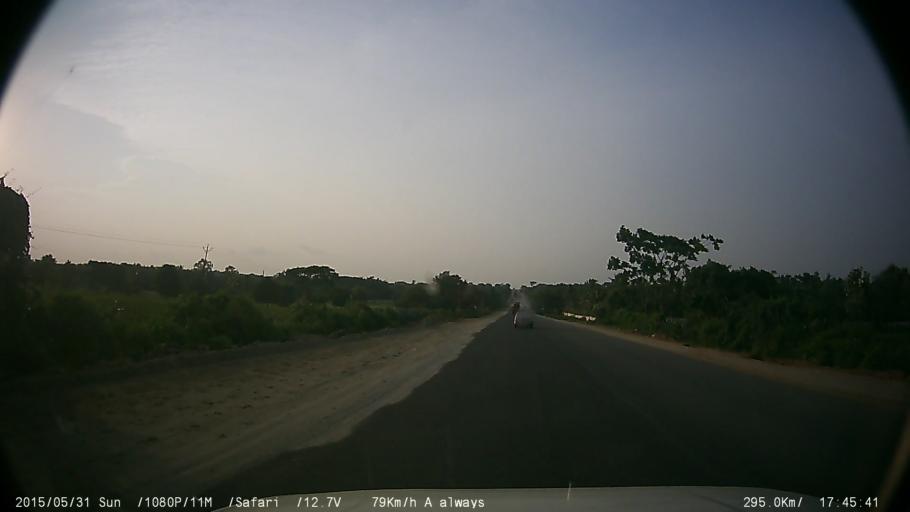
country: IN
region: Karnataka
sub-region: Chamrajnagar
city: Gundlupet
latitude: 11.9523
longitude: 76.6707
